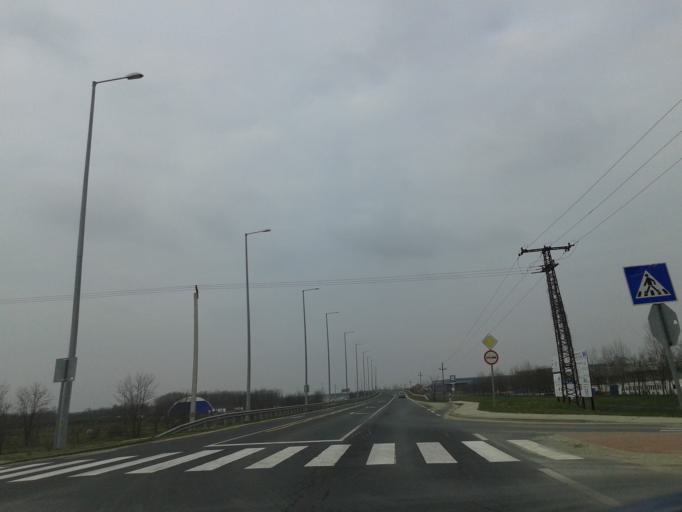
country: HU
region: Gyor-Moson-Sopron
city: Toltestava
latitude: 47.7322
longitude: 17.7820
